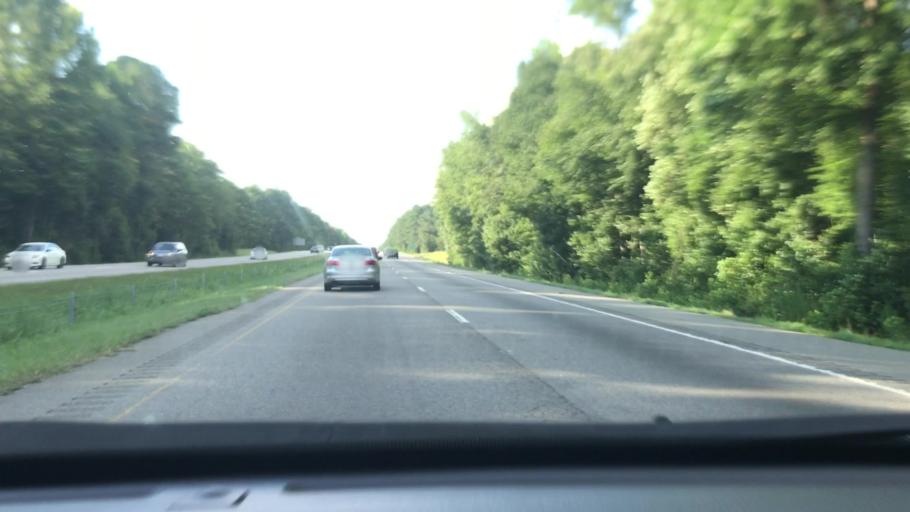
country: US
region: North Carolina
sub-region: Robeson County
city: Saint Pauls
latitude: 34.7294
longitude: -78.9972
